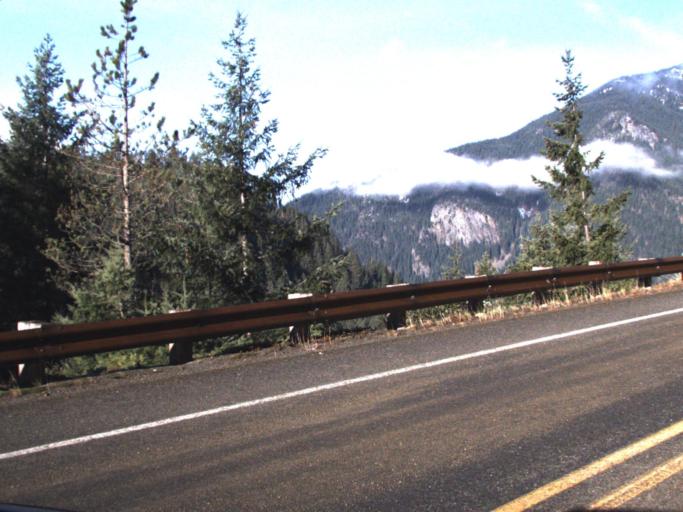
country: US
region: Washington
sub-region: Snohomish County
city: Darrington
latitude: 48.7006
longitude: -121.0965
